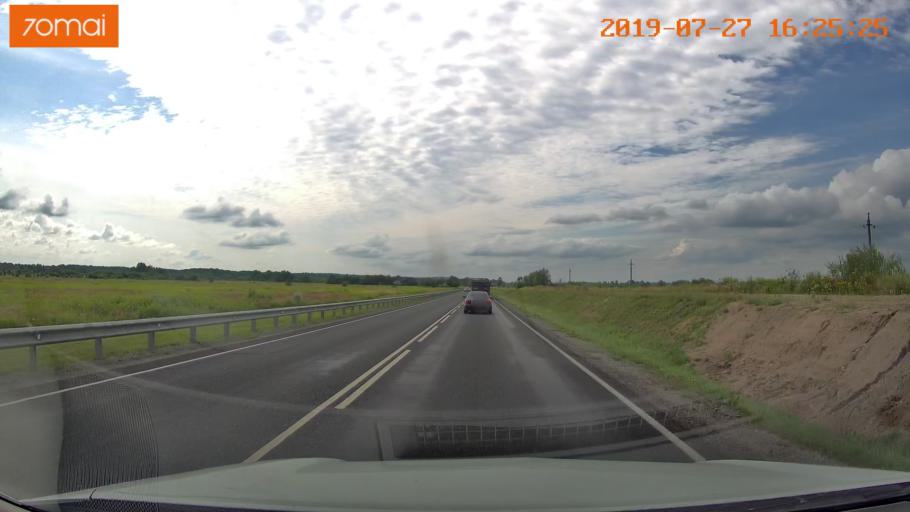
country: RU
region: Kaliningrad
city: Zheleznodorozhnyy
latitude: 54.6372
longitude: 21.4317
